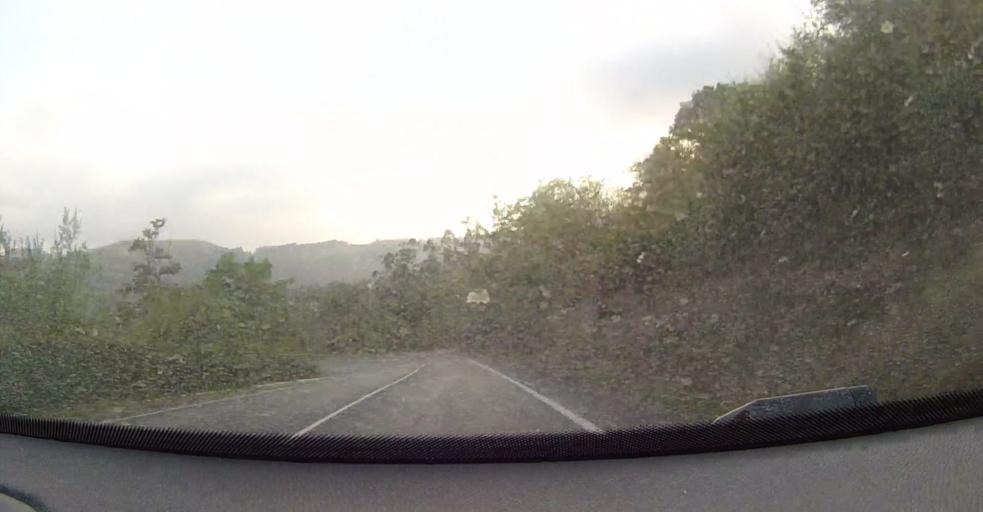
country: ES
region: Basque Country
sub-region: Bizkaia
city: Sopuerta
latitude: 43.2845
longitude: -3.1616
